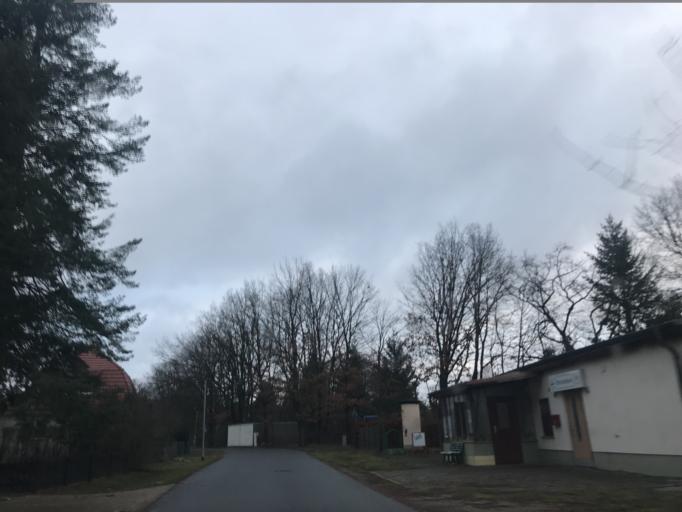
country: DE
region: Brandenburg
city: Rheinsberg
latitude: 53.0921
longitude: 12.8960
